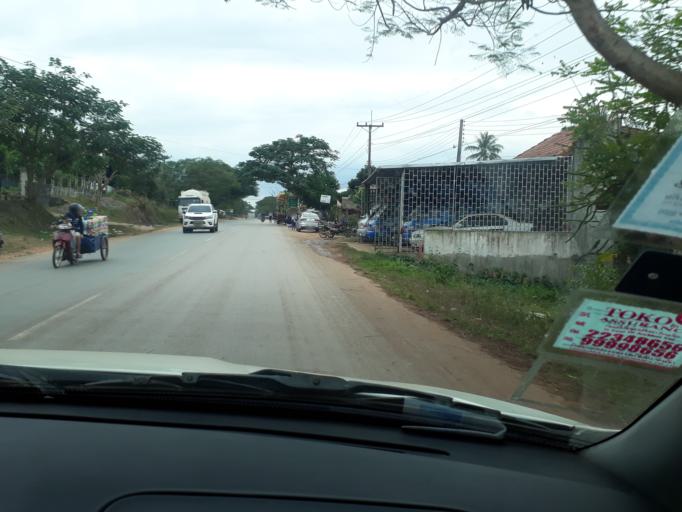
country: LA
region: Vientiane
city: Muang Phon-Hong
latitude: 18.3301
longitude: 102.4431
